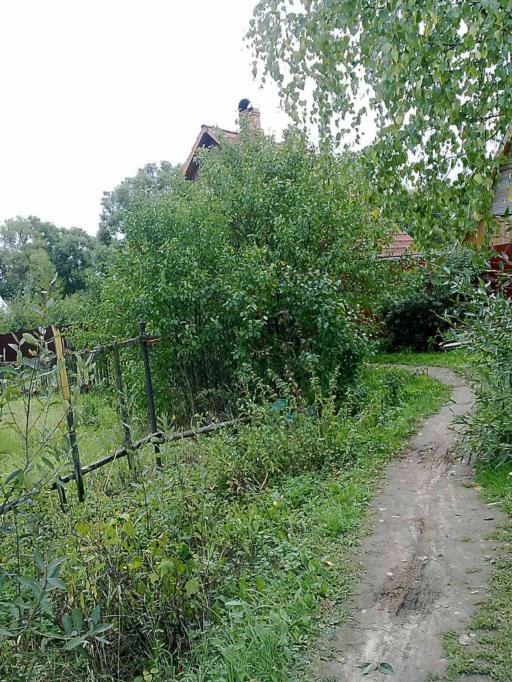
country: RU
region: Moskovskaya
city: Lesnoy Gorodok
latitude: 55.6514
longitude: 37.2094
